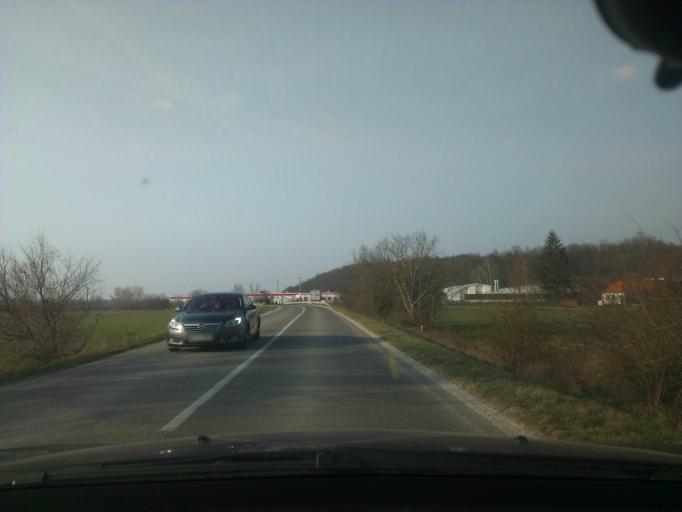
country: SK
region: Trnavsky
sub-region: Okres Trnava
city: Piestany
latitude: 48.6634
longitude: 17.8770
